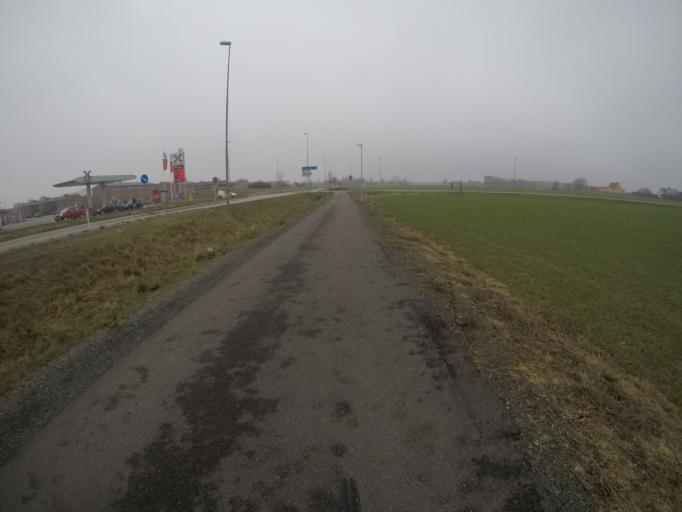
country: SE
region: Skane
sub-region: Hoganas Kommun
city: Hoganas
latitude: 56.2032
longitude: 12.5774
